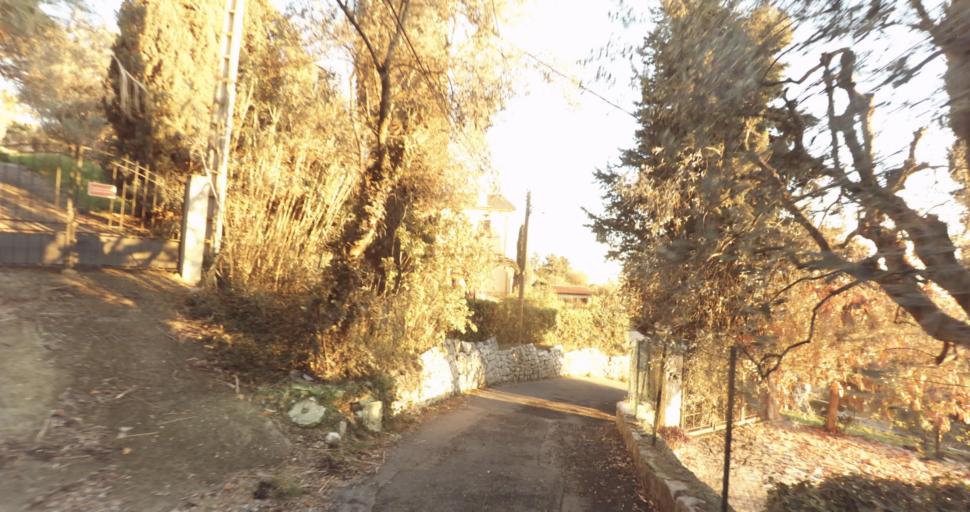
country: FR
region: Provence-Alpes-Cote d'Azur
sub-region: Departement des Alpes-Maritimes
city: Vence
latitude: 43.7286
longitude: 7.1068
